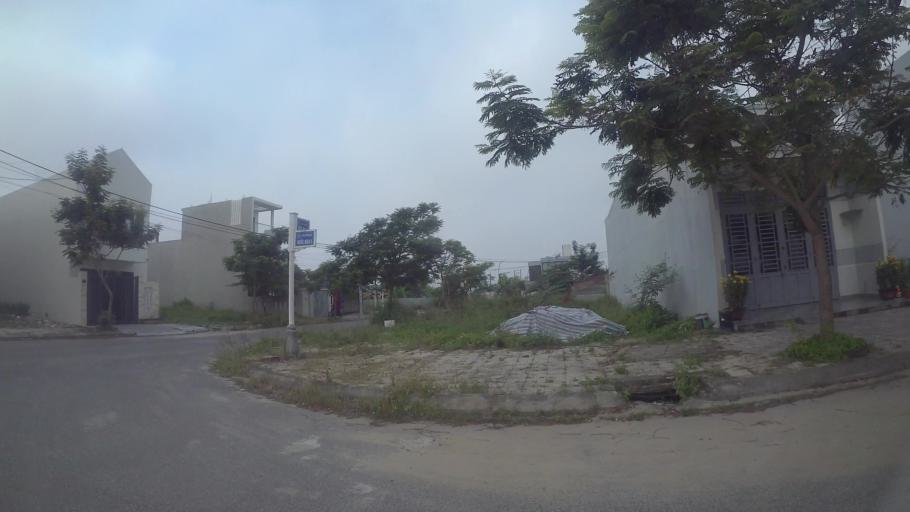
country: VN
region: Da Nang
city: Ngu Hanh Son
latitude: 16.0210
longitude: 108.2459
